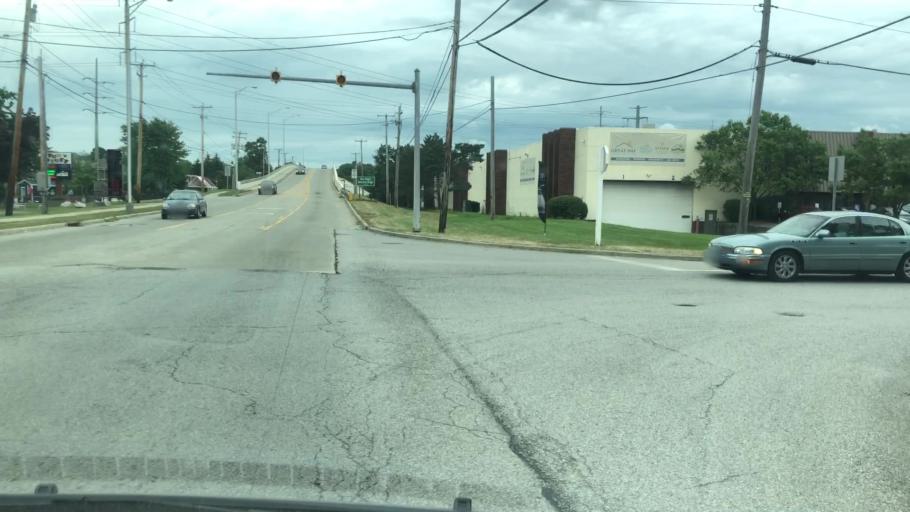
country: US
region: Ohio
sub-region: Summit County
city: Macedonia
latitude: 41.2990
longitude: -81.5022
